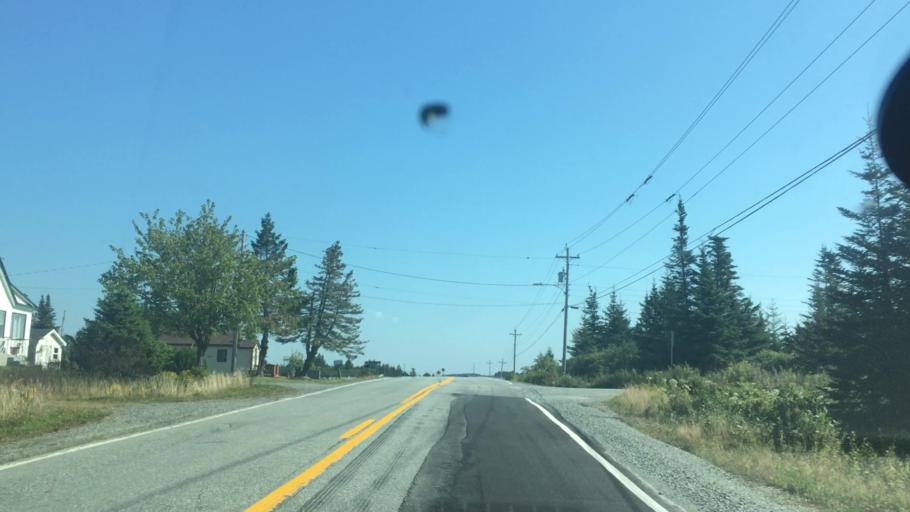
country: CA
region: Nova Scotia
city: New Glasgow
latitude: 44.9169
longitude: -62.3101
